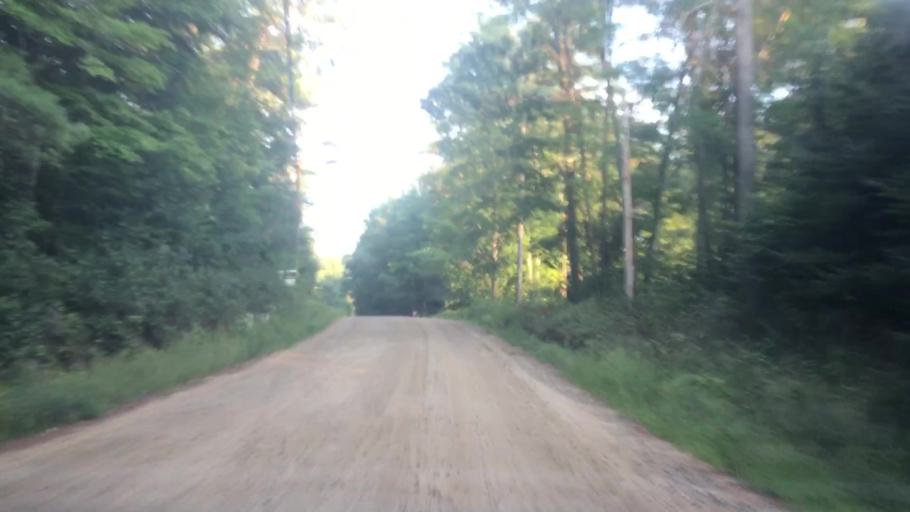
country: US
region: New Hampshire
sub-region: Belknap County
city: Barnstead
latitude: 43.4180
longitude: -71.2899
